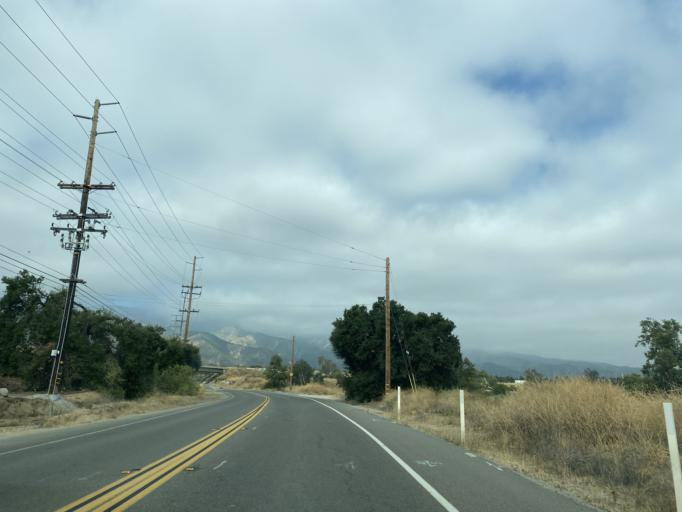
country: US
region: California
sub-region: Riverside County
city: El Cerrito
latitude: 33.7631
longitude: -117.4687
